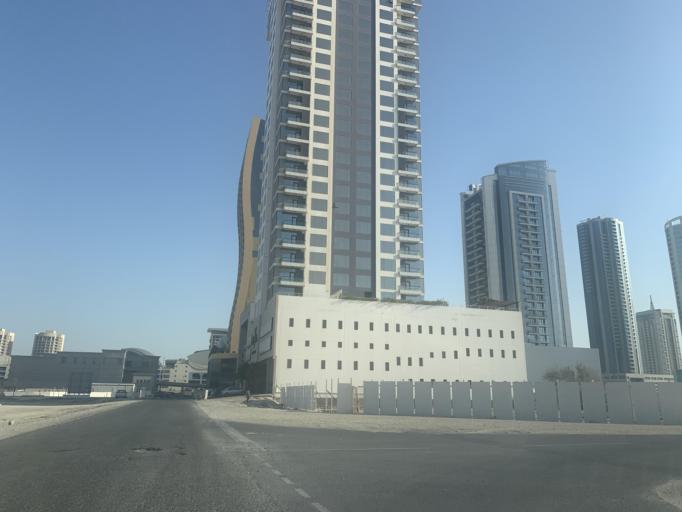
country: BH
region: Manama
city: Jidd Hafs
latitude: 26.2380
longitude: 50.5533
